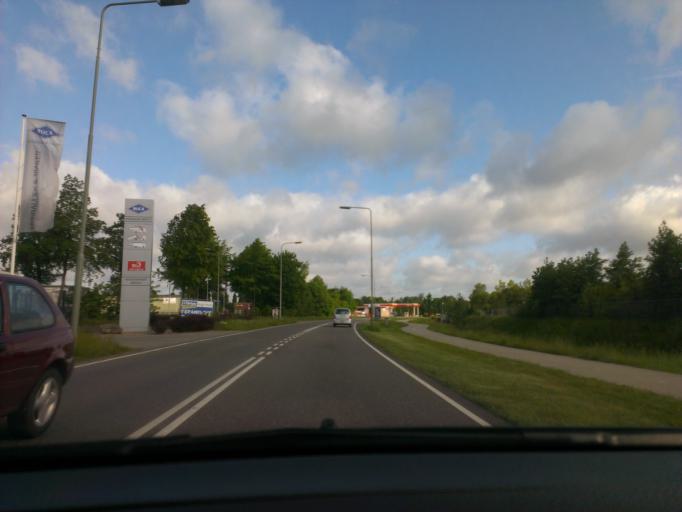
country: NL
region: Limburg
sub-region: Gemeente Heerlen
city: Nieuw-Lotbroek
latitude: 50.9072
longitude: 5.9389
